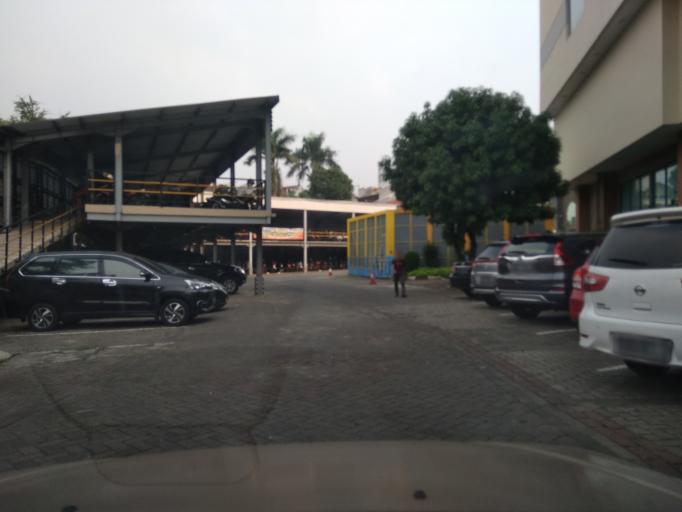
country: ID
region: West Java
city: Serpong
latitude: -6.2793
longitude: 106.6632
